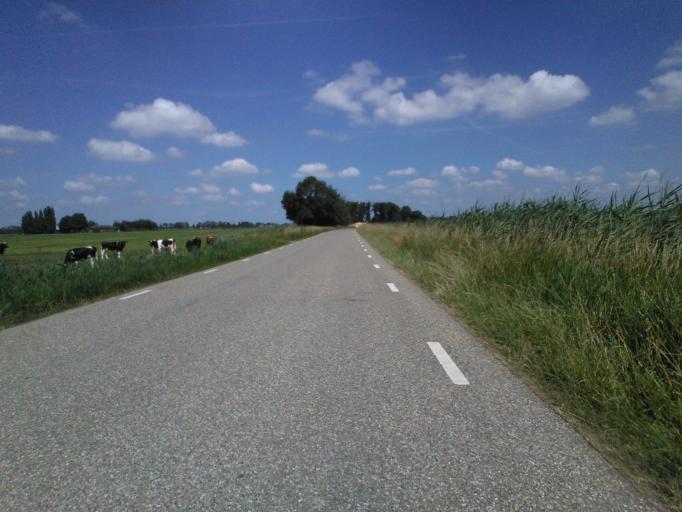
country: NL
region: North Brabant
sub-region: Gemeente Woudrichem
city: Almkerk
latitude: 51.7487
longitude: 4.9709
